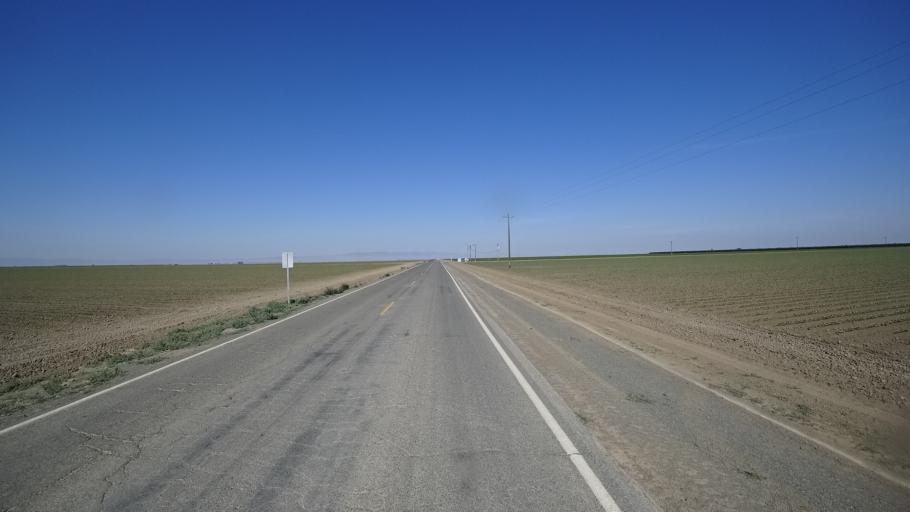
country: US
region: California
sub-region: Fresno County
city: Riverdale
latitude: 36.3863
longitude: -119.9569
